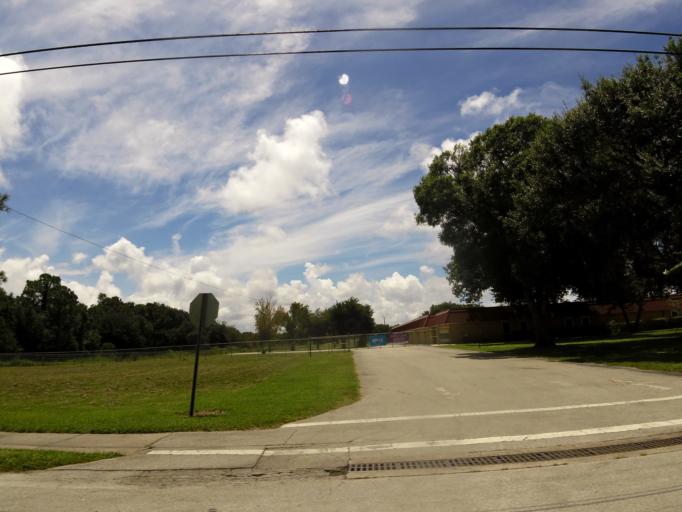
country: US
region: Florida
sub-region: Brevard County
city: Mims
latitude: 28.6371
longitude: -80.8488
